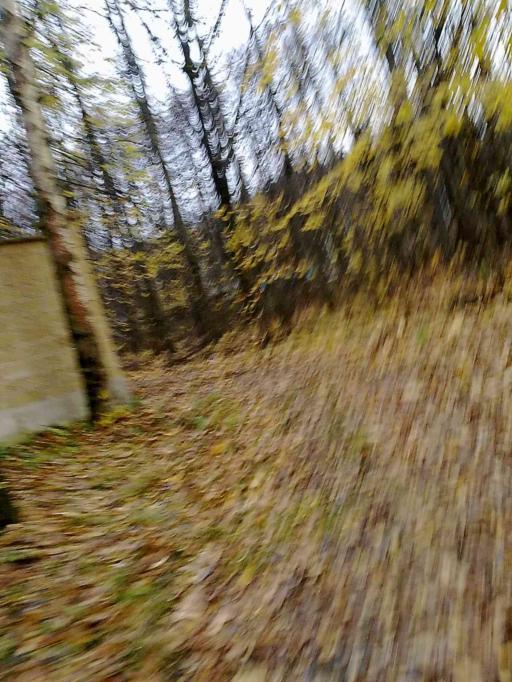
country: RU
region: Moscow
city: Novo-Peredelkino
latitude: 55.6467
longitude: 37.3118
